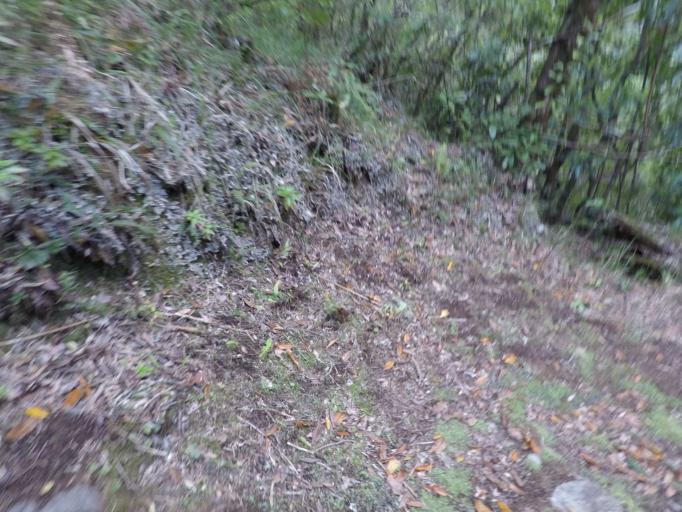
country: PT
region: Madeira
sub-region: Camara de Lobos
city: Curral das Freiras
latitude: 32.7712
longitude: -16.9781
